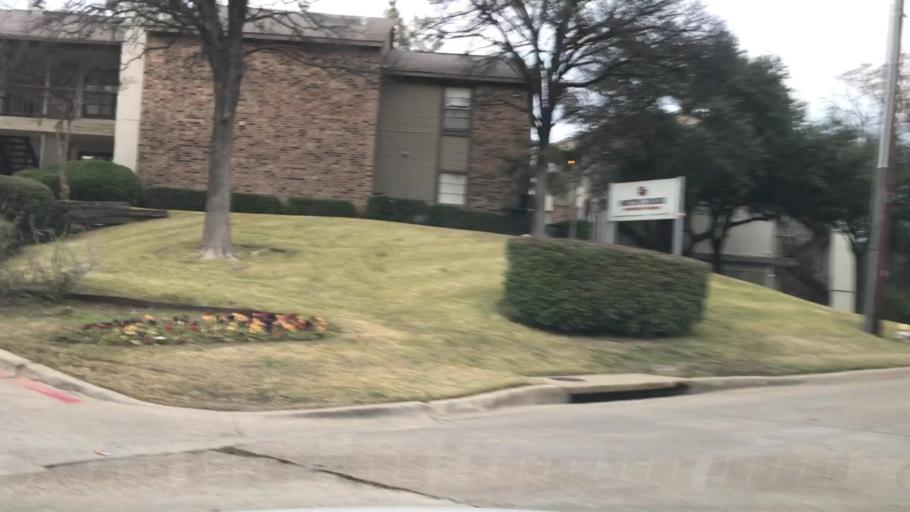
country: US
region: Texas
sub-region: Dallas County
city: Duncanville
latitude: 32.6912
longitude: -96.9033
